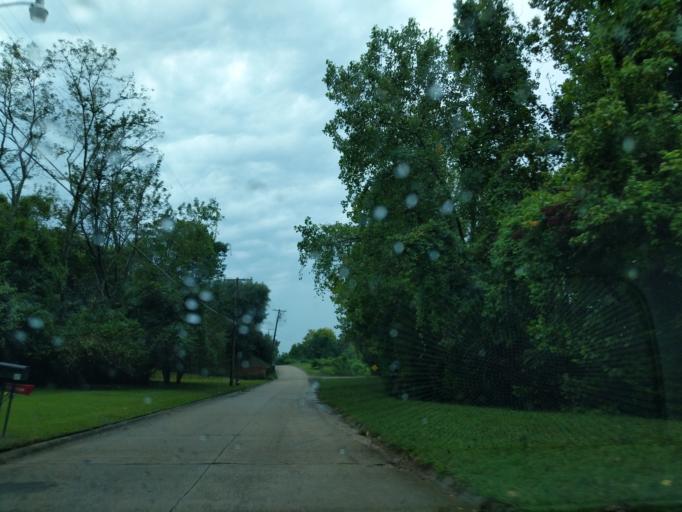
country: US
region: Mississippi
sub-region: Warren County
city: Vicksburg
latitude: 32.3641
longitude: -90.8724
